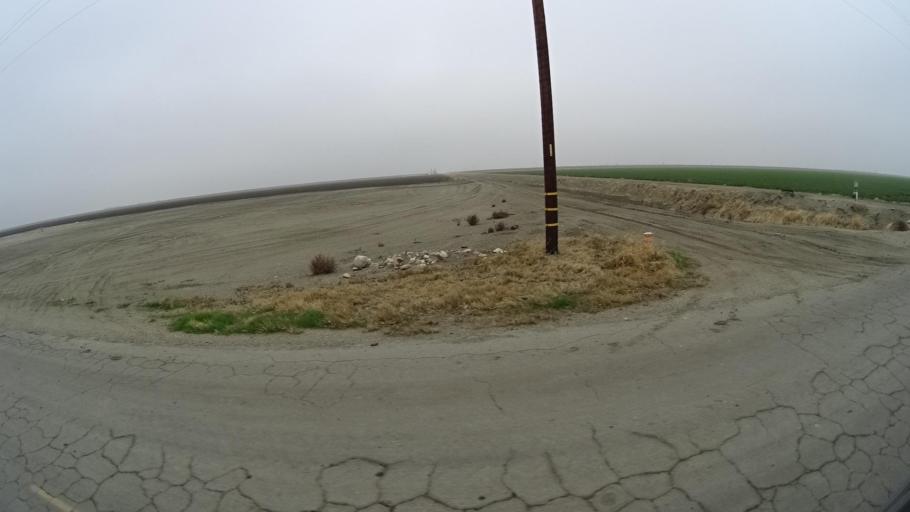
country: US
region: California
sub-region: Kern County
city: Rosedale
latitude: 35.1944
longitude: -119.2217
